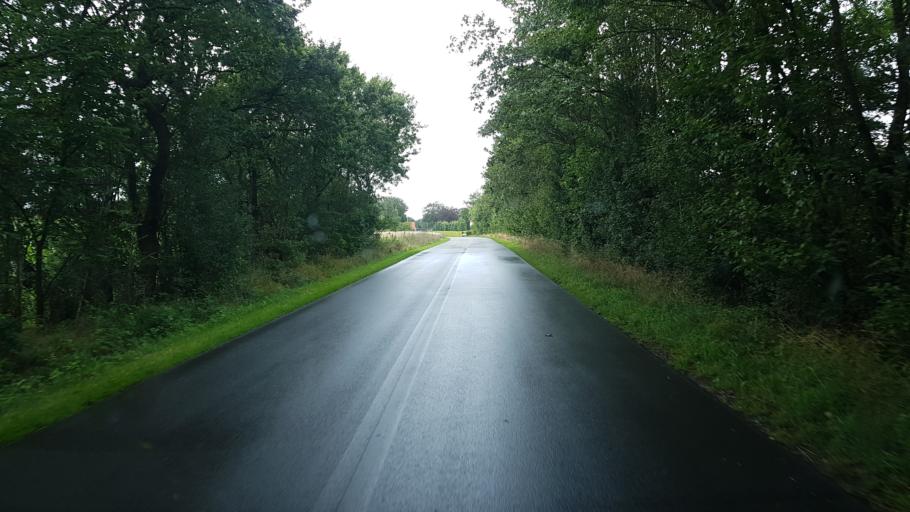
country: DK
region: South Denmark
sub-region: Vejen Kommune
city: Holsted
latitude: 55.5989
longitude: 8.8100
